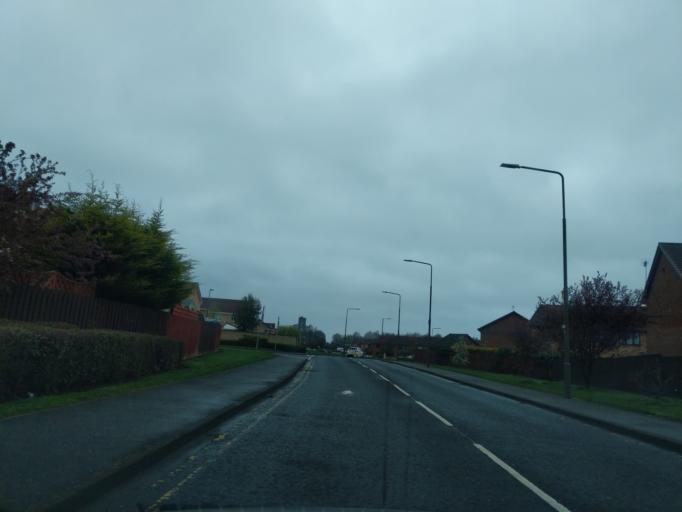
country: GB
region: Scotland
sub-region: East Lothian
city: Musselburgh
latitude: 55.9354
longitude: -3.0729
